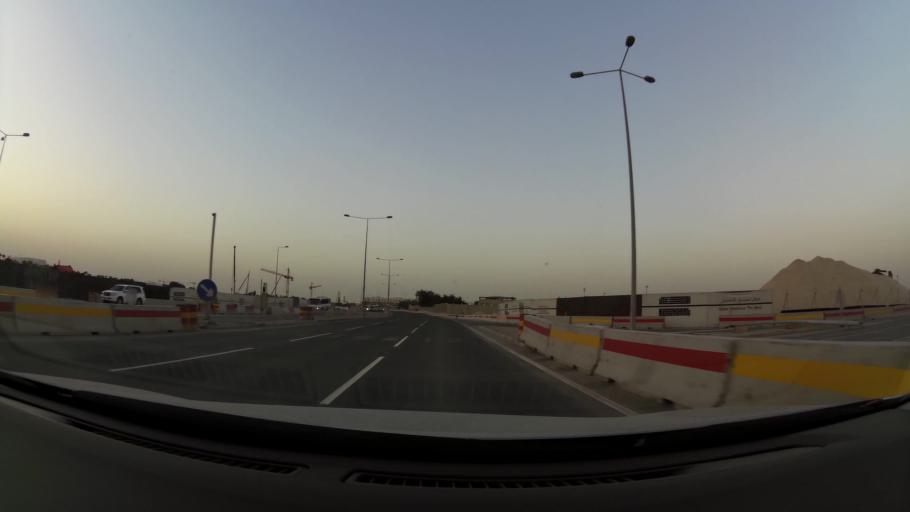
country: QA
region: Baladiyat ar Rayyan
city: Ar Rayyan
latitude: 25.2943
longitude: 51.4661
